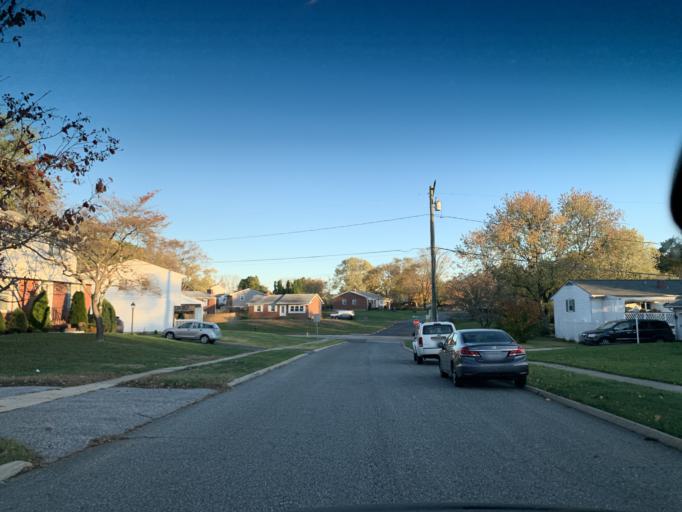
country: US
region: Maryland
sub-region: Harford County
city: Bel Air North
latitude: 39.5585
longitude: -76.3759
